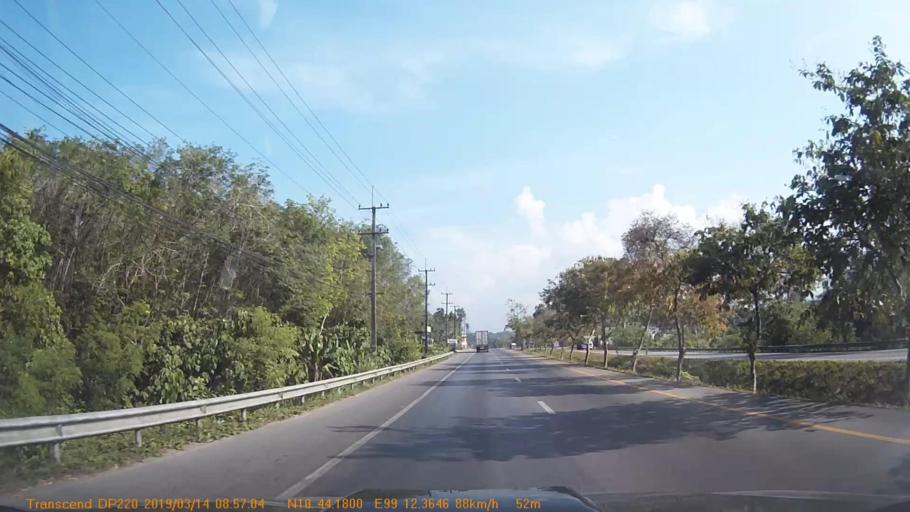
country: TH
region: Chumphon
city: Tha Sae
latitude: 10.7367
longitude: 99.2061
